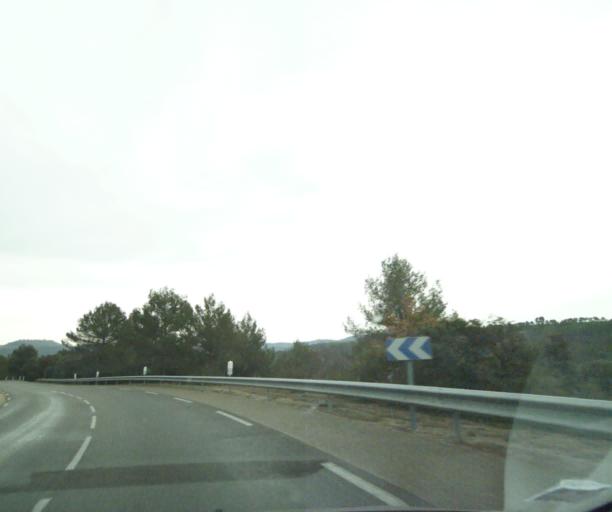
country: FR
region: Provence-Alpes-Cote d'Azur
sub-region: Departement des Bouches-du-Rhone
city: Rognes
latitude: 43.6598
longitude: 5.3899
